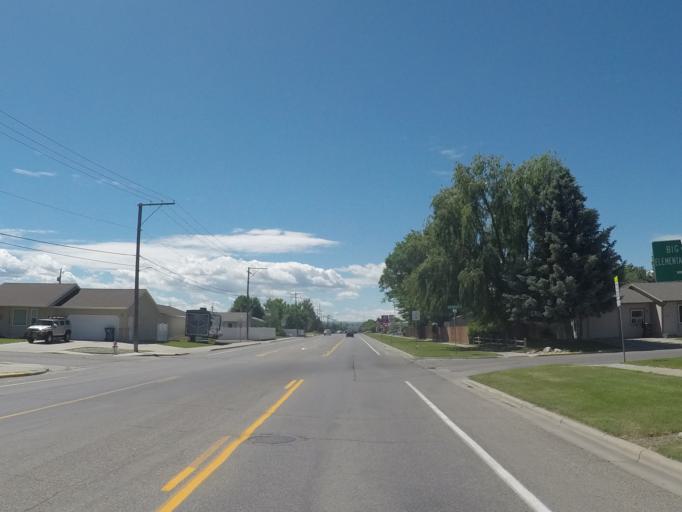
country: US
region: Montana
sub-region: Yellowstone County
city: Billings
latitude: 45.7591
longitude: -108.5969
